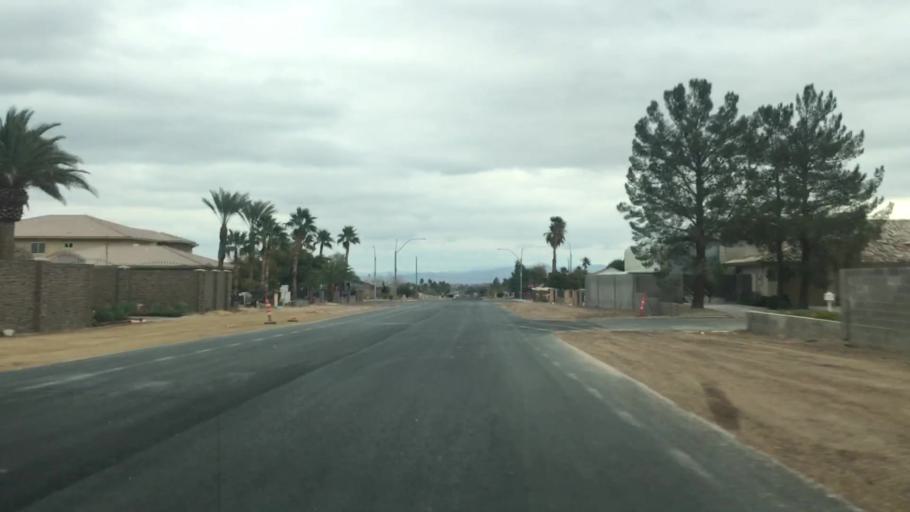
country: US
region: Nevada
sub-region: Clark County
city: Paradise
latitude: 36.0496
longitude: -115.1564
